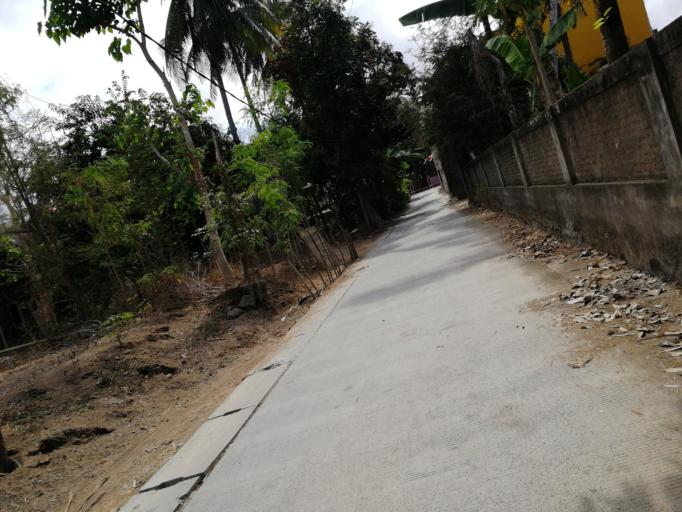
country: ID
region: West Nusa Tenggara
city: Kute
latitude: -8.8829
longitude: 116.2734
